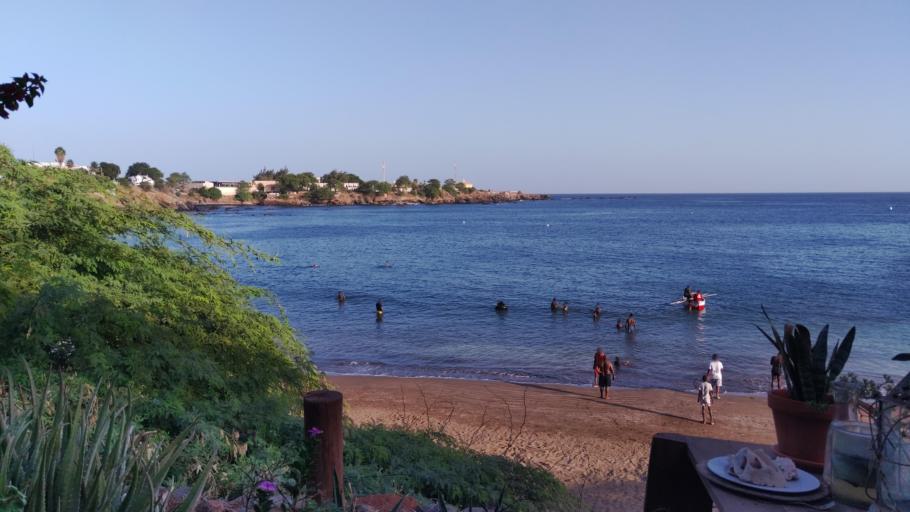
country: CV
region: Praia
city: Praia
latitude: 14.9036
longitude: -23.5178
